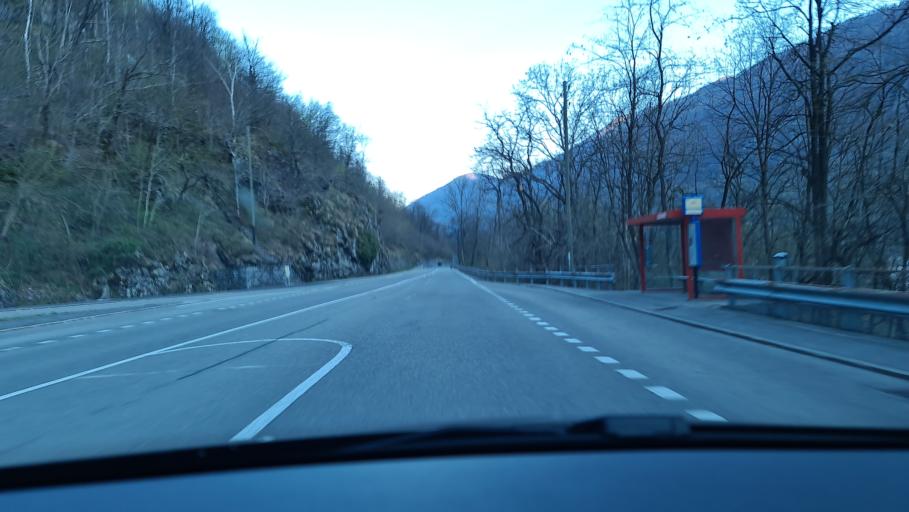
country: CH
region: Ticino
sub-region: Locarno District
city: Verscio
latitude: 46.2611
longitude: 8.6901
